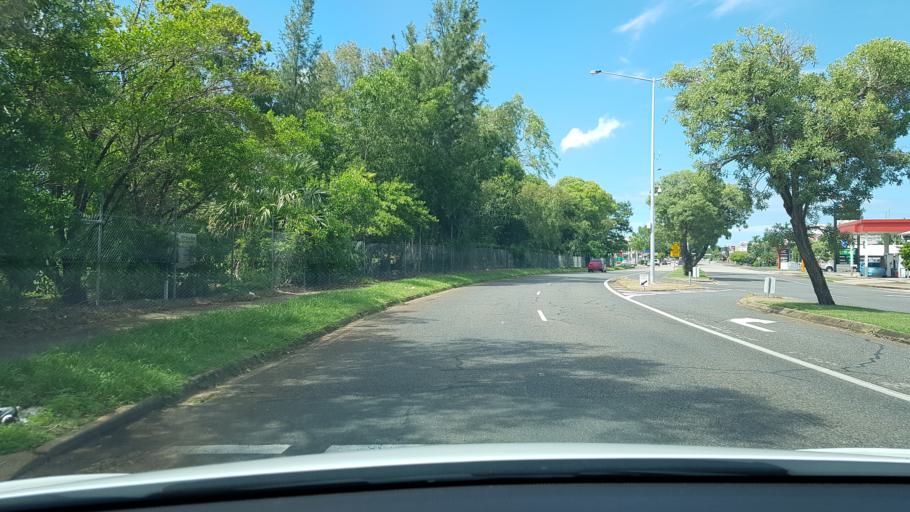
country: AU
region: Northern Territory
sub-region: Darwin
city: Leanyer
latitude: -12.3714
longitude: 130.8841
